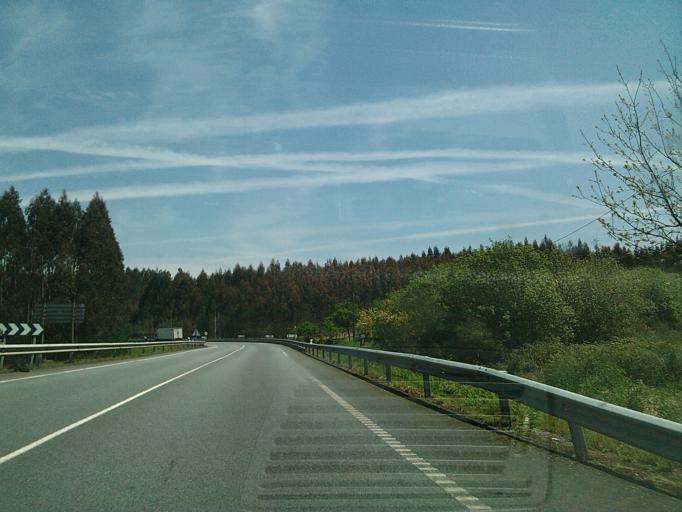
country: ES
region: Galicia
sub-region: Provincia da Coruna
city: Mesia
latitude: 43.0526
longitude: -8.2128
